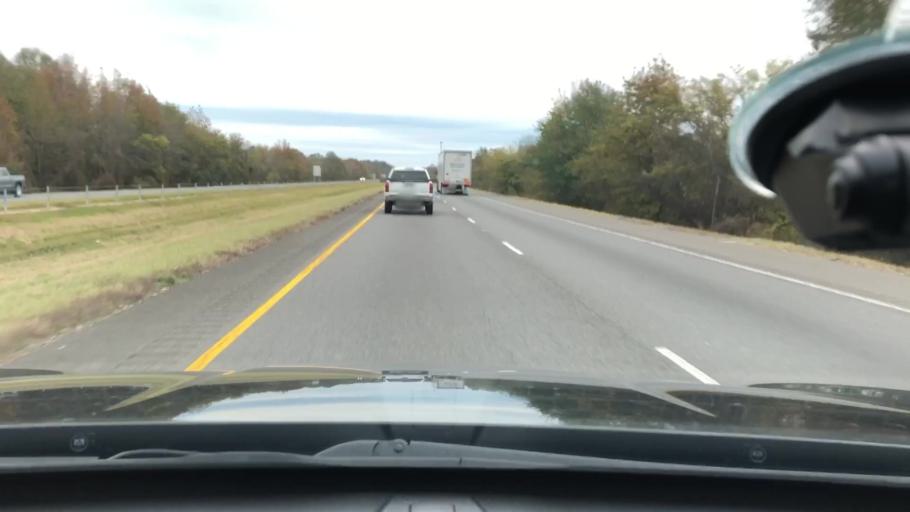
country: US
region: Arkansas
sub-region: Clark County
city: Gurdon
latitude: 34.0057
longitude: -93.1749
